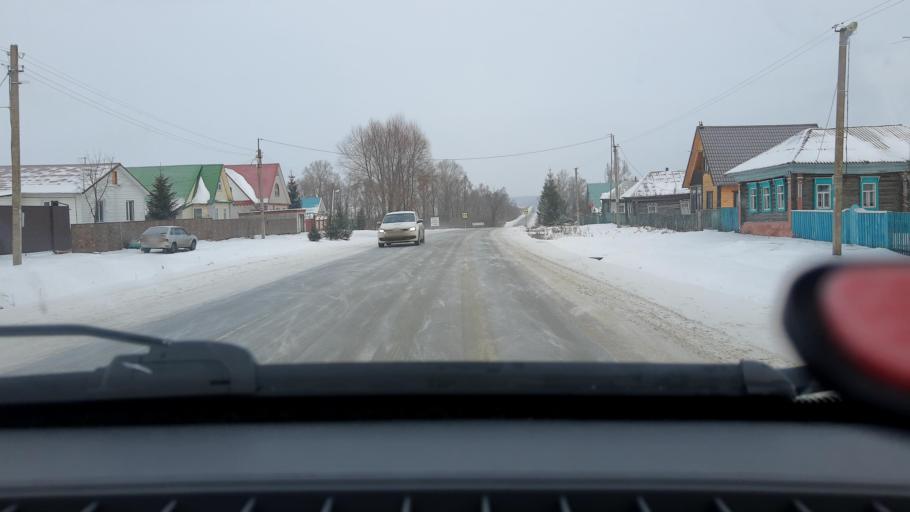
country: RU
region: Bashkortostan
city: Iglino
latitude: 54.7390
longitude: 56.3966
